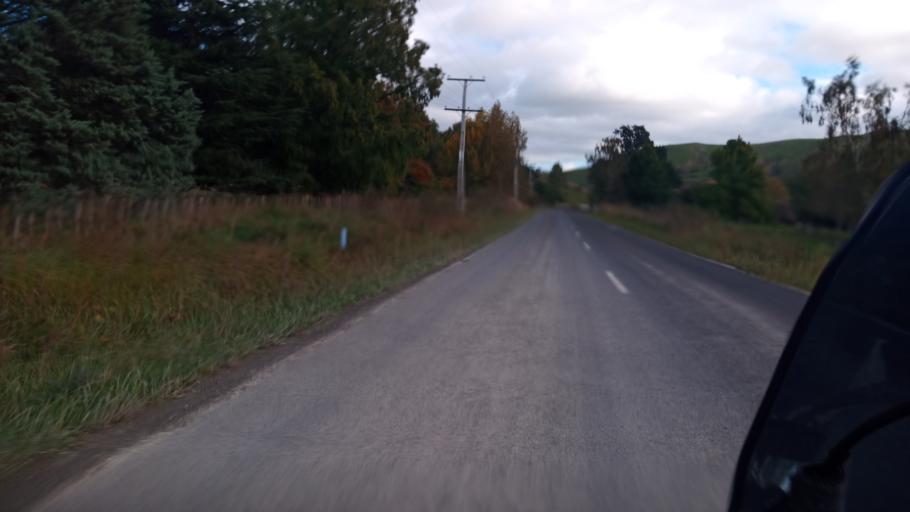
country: NZ
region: Gisborne
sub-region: Gisborne District
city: Gisborne
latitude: -38.5784
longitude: 177.7421
